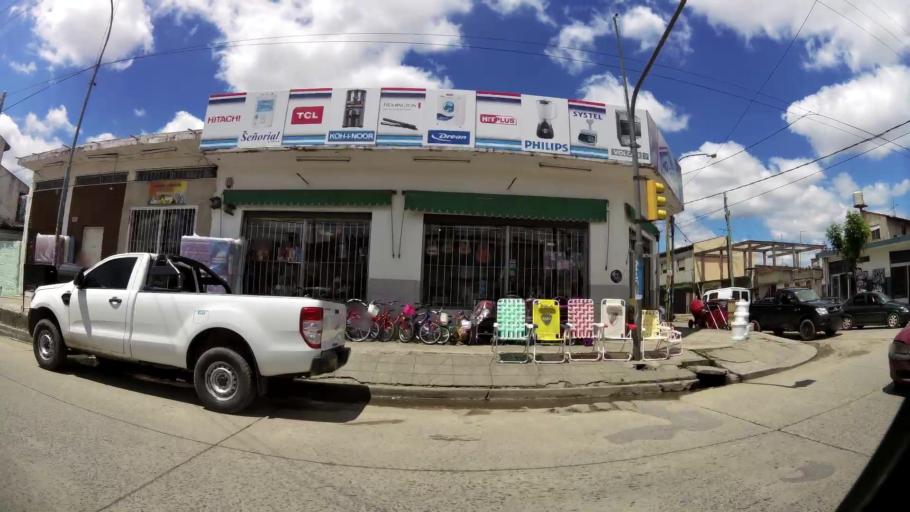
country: AR
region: Buenos Aires
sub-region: Partido de Lanus
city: Lanus
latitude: -34.7049
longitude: -58.4329
